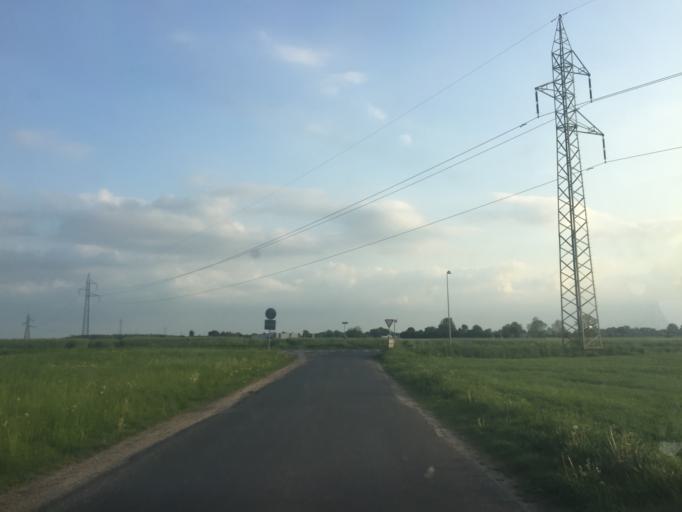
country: DK
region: South Denmark
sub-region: Faaborg-Midtfyn Kommune
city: Arslev
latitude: 55.3412
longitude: 10.5184
